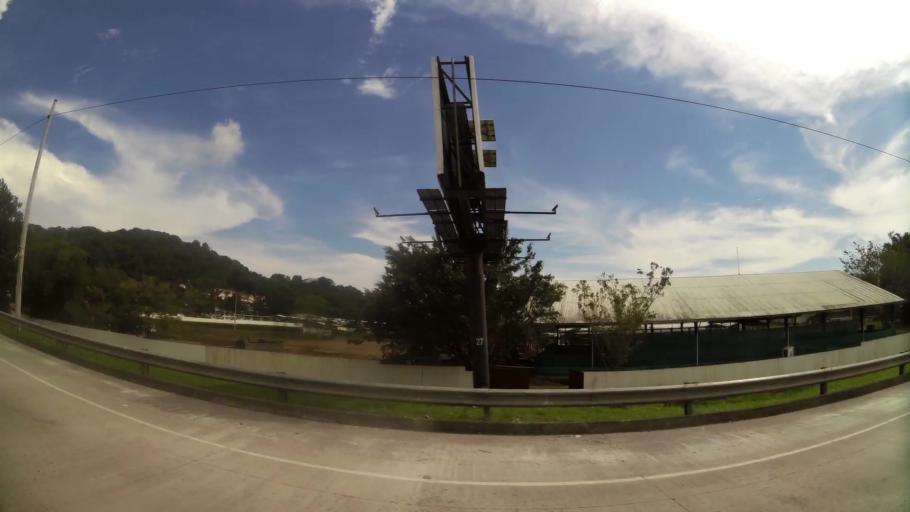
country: PA
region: Panama
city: San Miguelito
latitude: 9.0802
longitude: -79.4722
